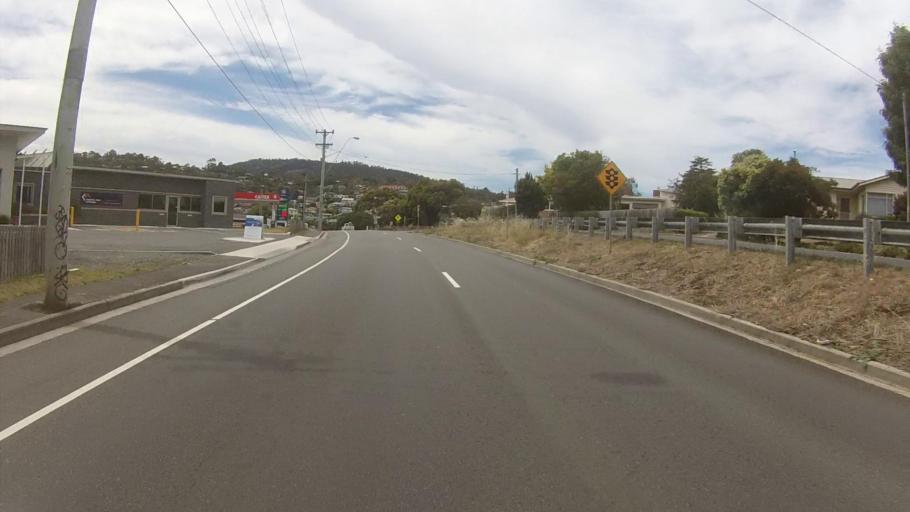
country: AU
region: Tasmania
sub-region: Clarence
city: Lindisfarne
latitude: -42.8522
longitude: 147.3598
